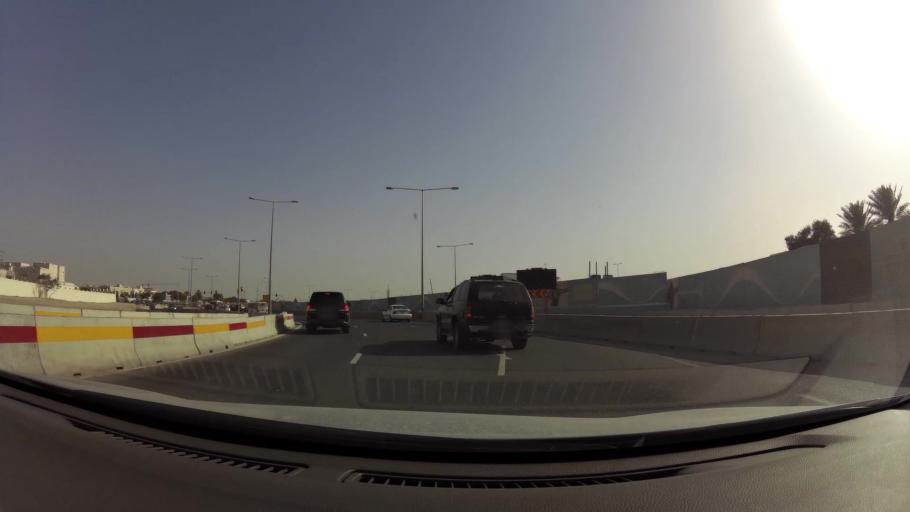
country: QA
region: Baladiyat ar Rayyan
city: Ar Rayyan
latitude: 25.3313
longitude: 51.4476
